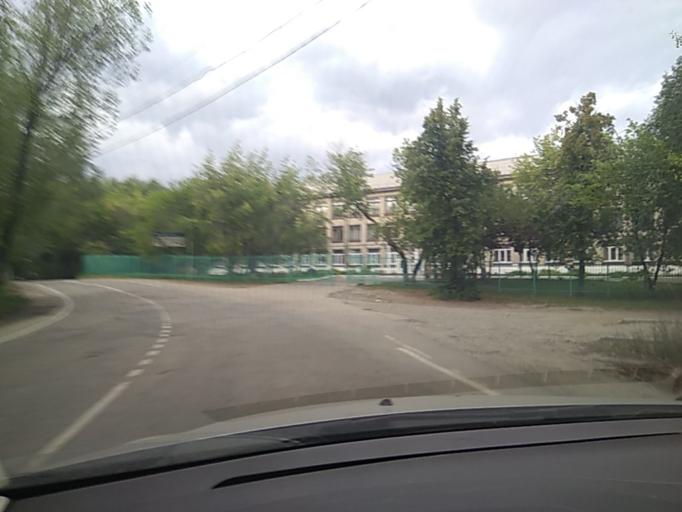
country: RU
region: Chelyabinsk
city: Kyshtym
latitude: 55.7023
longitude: 60.5307
